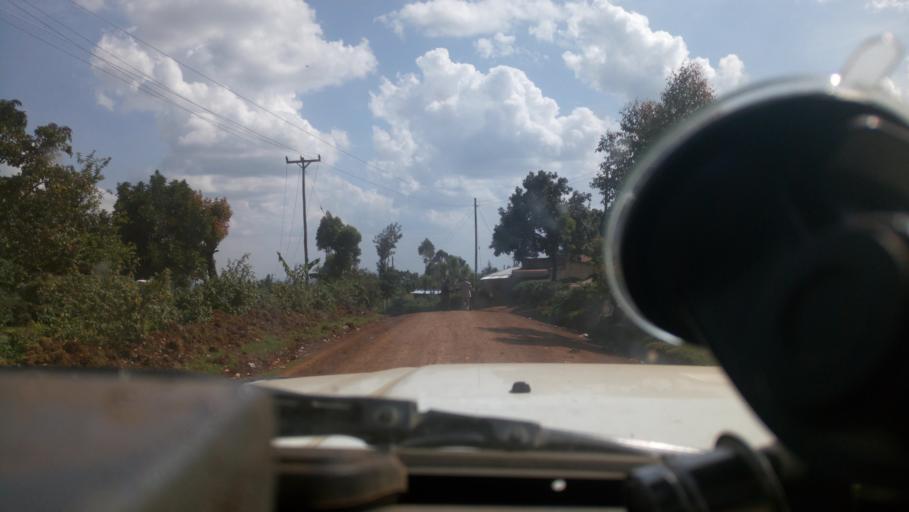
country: KE
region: Nyamira District
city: Nyamira
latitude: -0.6700
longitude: 34.8706
